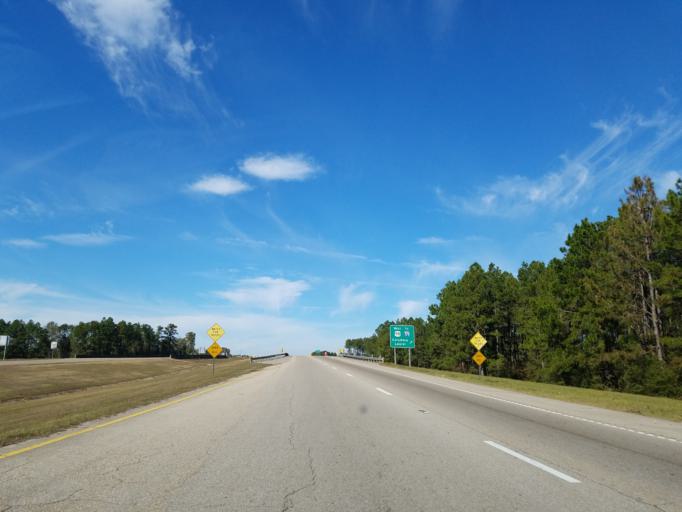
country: US
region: Mississippi
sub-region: Forrest County
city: Hattiesburg
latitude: 31.2432
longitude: -89.2750
